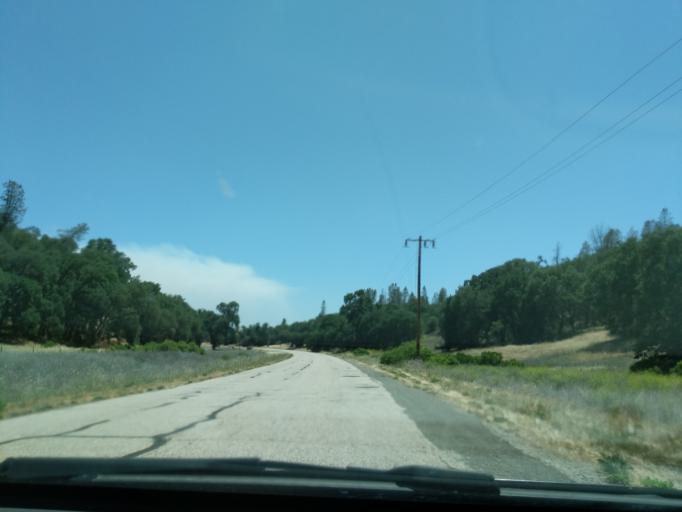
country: US
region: California
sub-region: Monterey County
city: King City
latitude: 36.0484
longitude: -121.1826
